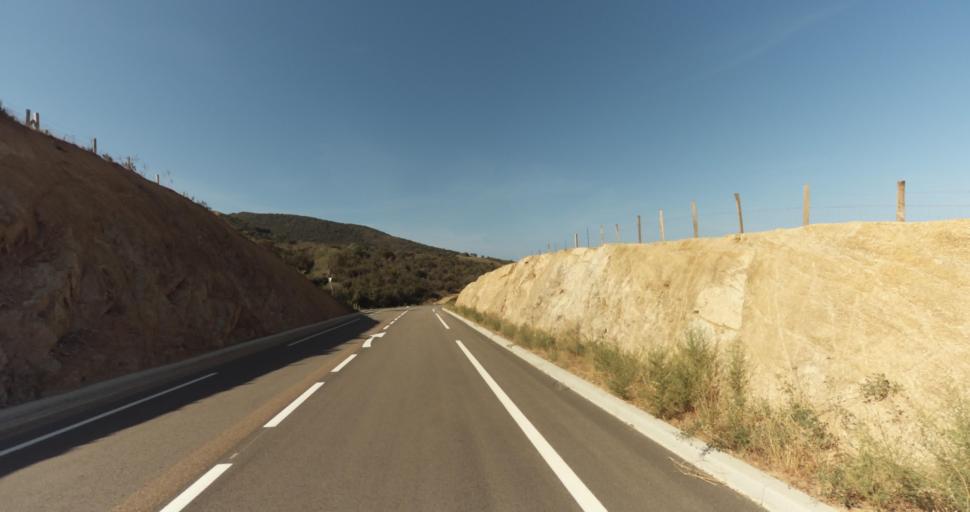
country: FR
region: Corsica
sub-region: Departement de la Corse-du-Sud
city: Ajaccio
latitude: 41.9302
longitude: 8.6509
